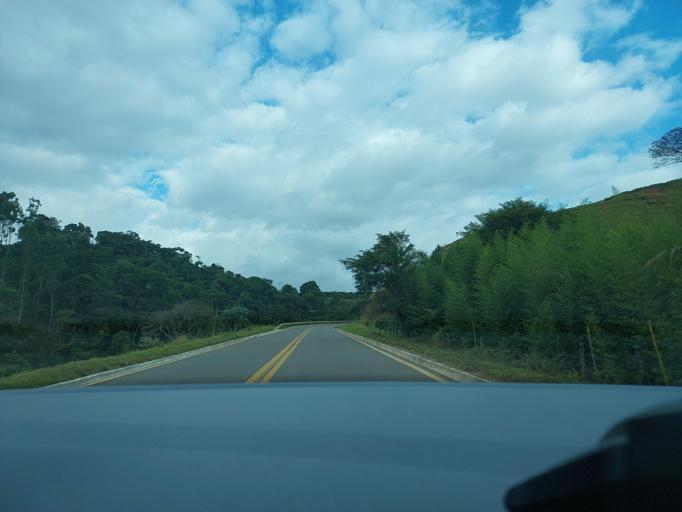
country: BR
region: Minas Gerais
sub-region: Visconde Do Rio Branco
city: Visconde do Rio Branco
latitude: -20.9384
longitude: -42.6278
